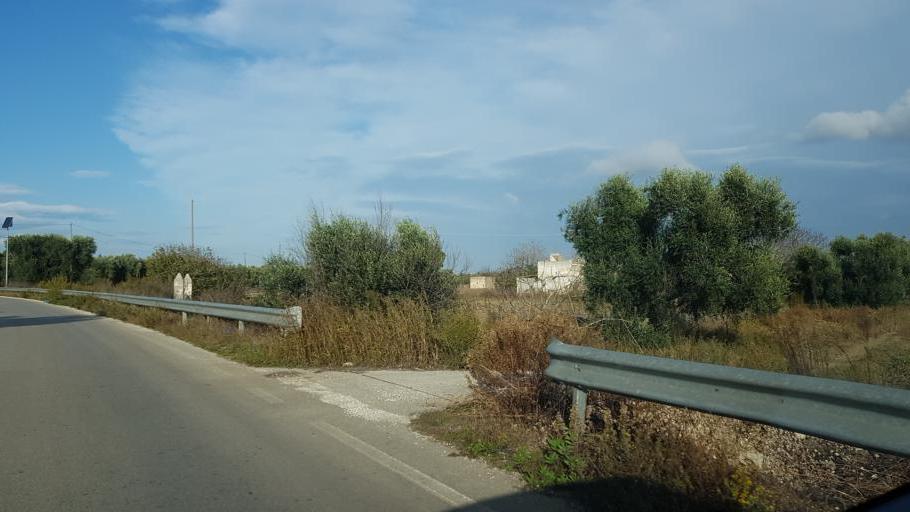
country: IT
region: Apulia
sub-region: Provincia di Brindisi
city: Oria
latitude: 40.5307
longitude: 17.6556
